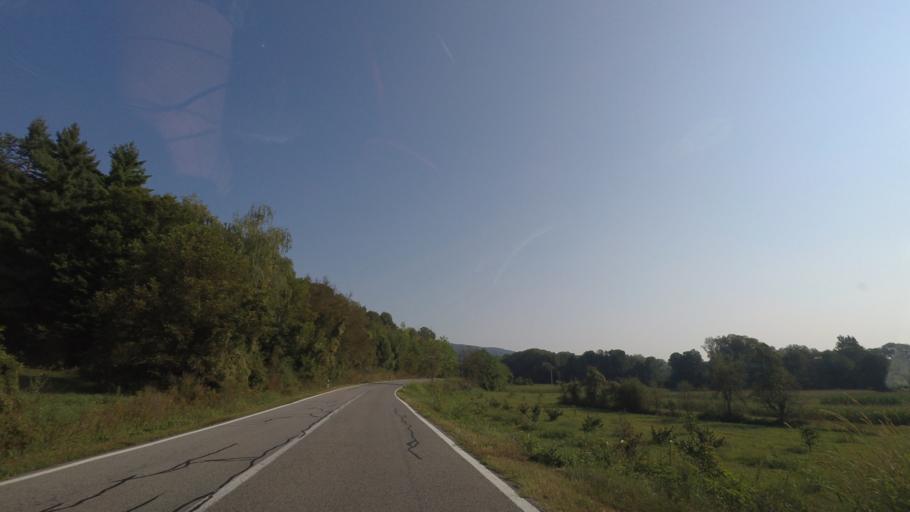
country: HR
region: Brodsko-Posavska
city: Resetari
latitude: 45.4151
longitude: 17.5003
